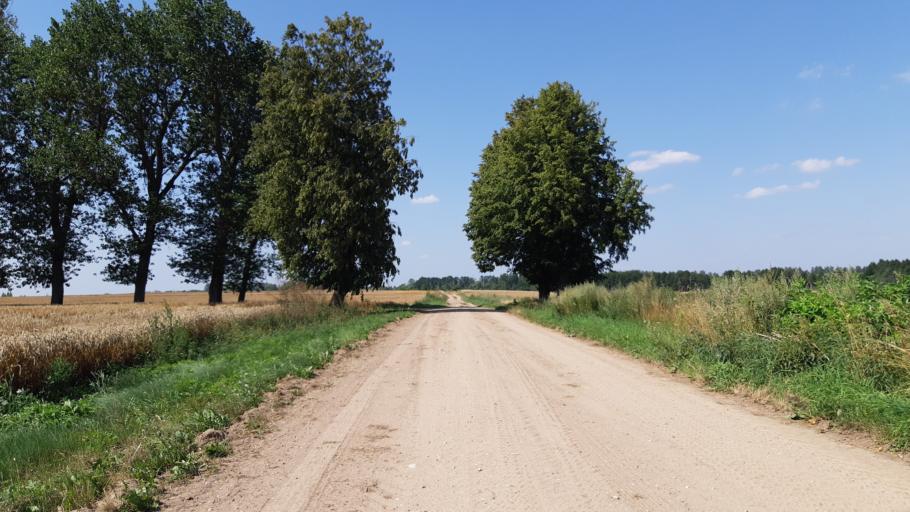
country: LT
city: Virbalis
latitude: 54.6394
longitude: 22.8217
